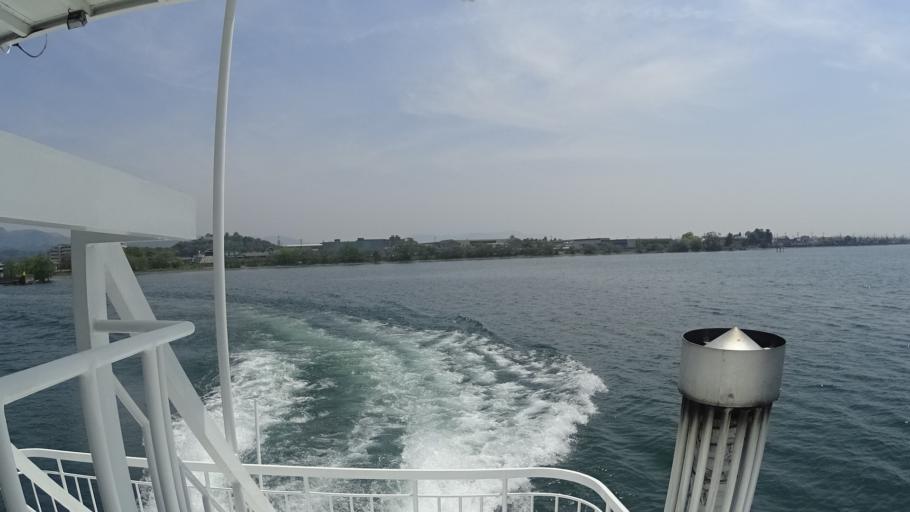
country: JP
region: Shiga Prefecture
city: Hikone
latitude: 35.2837
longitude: 136.2422
